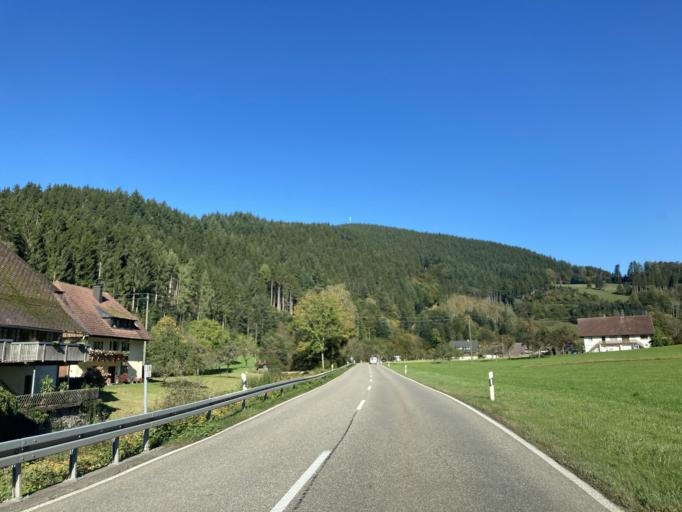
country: DE
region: Baden-Wuerttemberg
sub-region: Freiburg Region
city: Oberwolfach
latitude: 48.3307
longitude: 8.2190
